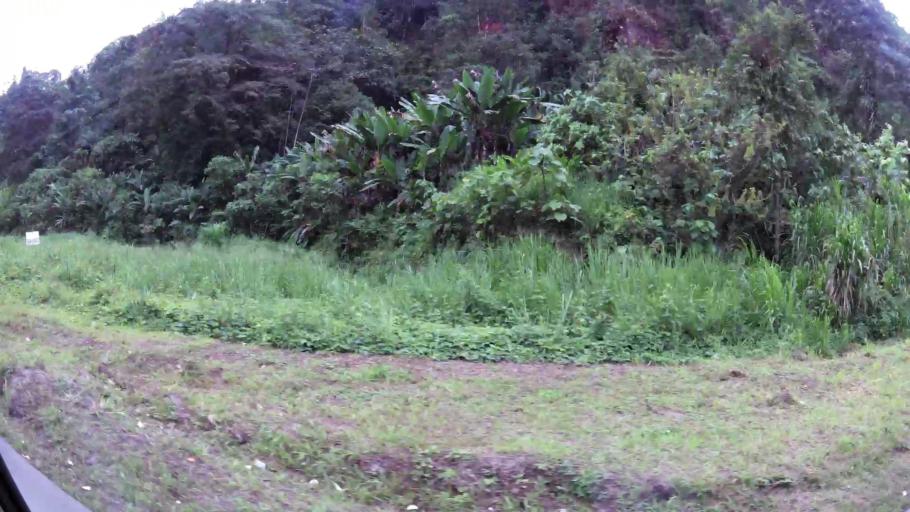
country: EC
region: Santo Domingo de los Tsachilas
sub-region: Canton Santo Domingo de los Colorados
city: Santo Domingo de los Colorados
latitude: -0.2738
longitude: -79.0797
